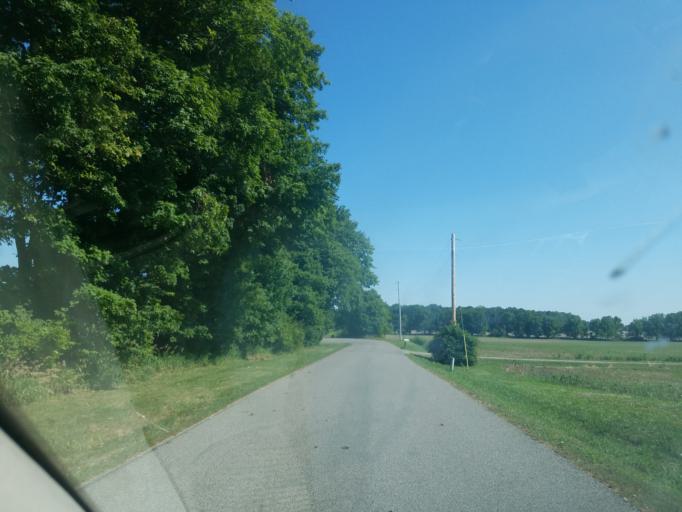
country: US
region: Ohio
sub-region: Logan County
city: Northwood
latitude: 40.4356
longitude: -83.6706
